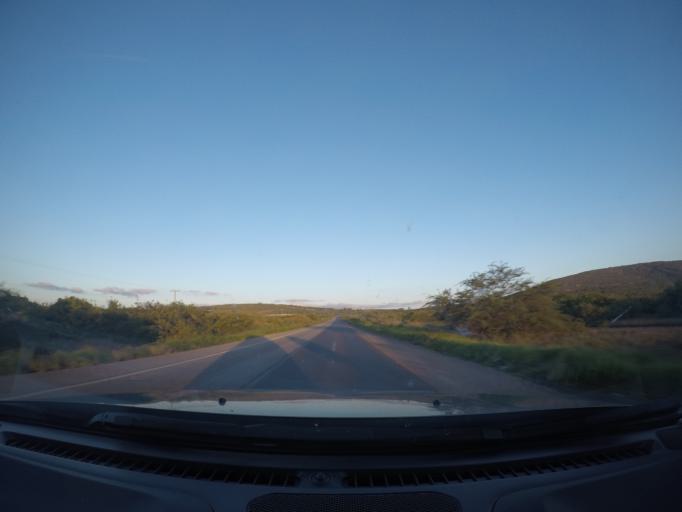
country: BR
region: Bahia
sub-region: Seabra
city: Seabra
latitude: -12.3899
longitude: -41.8984
